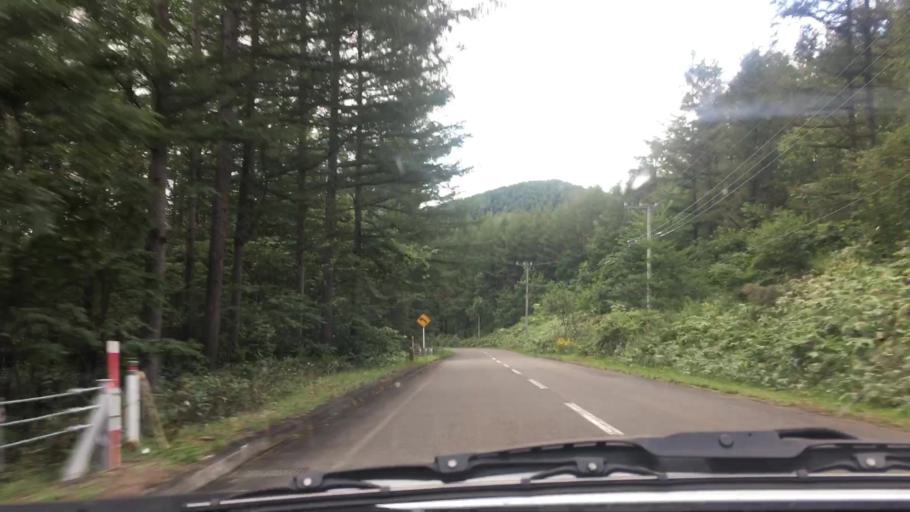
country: JP
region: Hokkaido
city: Otofuke
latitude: 43.1541
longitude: 142.8580
